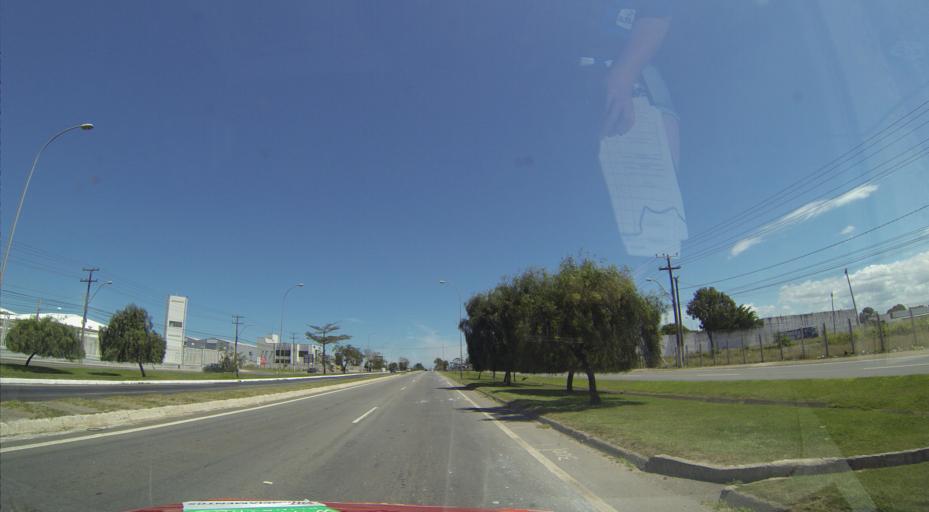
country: BR
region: Espirito Santo
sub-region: Serra
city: Serra
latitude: -20.2016
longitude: -40.2691
